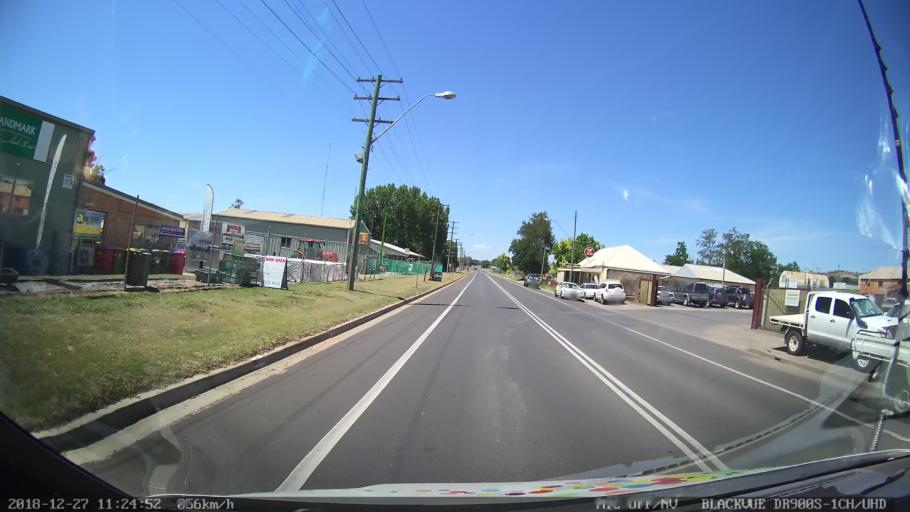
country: AU
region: New South Wales
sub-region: Bathurst Regional
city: Bathurst
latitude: -33.4369
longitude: 149.5785
